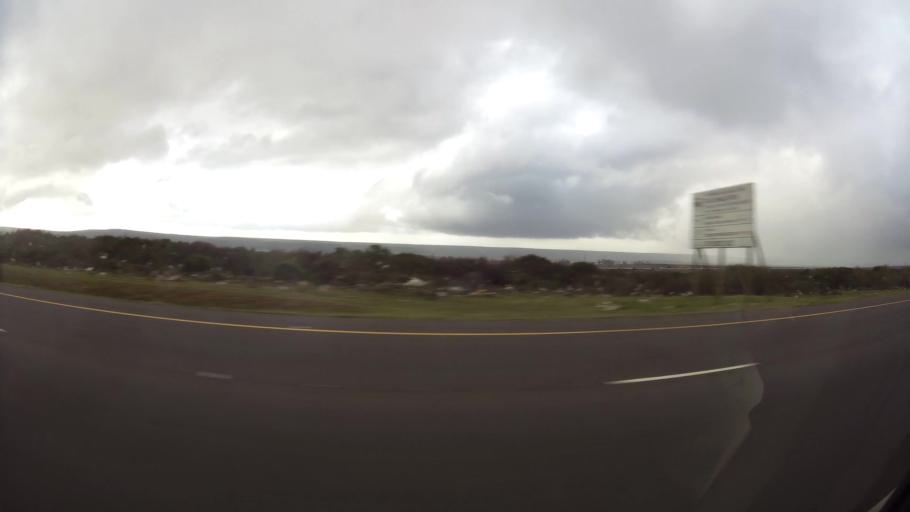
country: ZA
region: Eastern Cape
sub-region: Nelson Mandela Bay Metropolitan Municipality
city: Port Elizabeth
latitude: -33.8198
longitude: 25.5034
